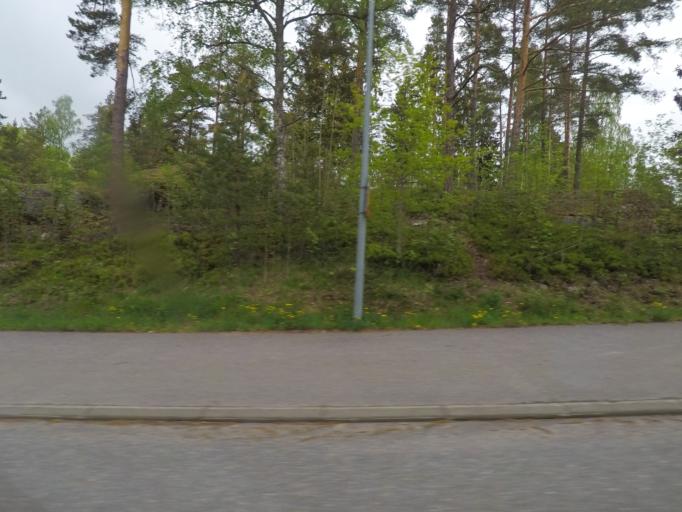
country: FI
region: Uusimaa
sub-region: Helsinki
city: Kirkkonummi
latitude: 60.1256
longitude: 24.4073
